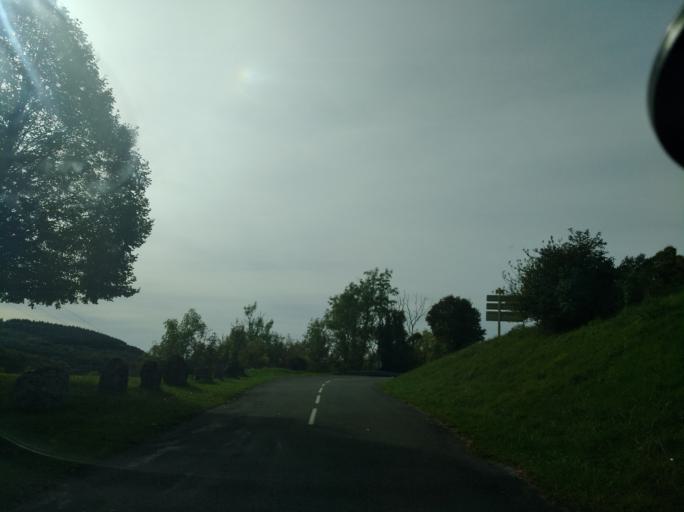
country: FR
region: Bourgogne
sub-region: Departement de Saone-et-Loire
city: Cuiseaux
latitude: 46.4572
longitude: 5.3821
